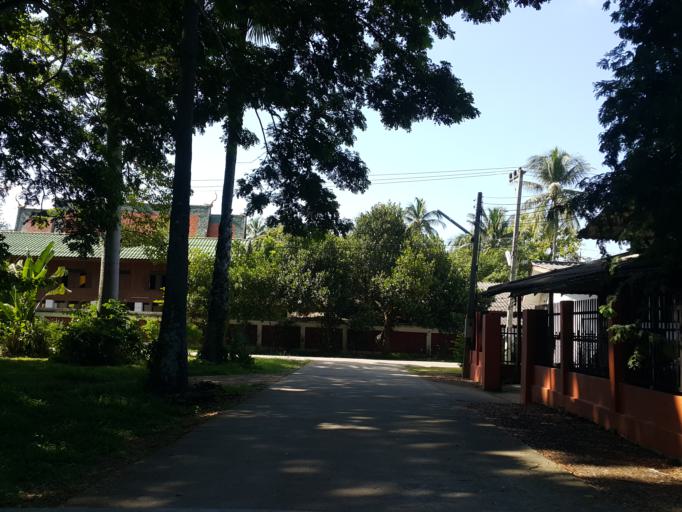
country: TH
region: Chiang Mai
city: San Kamphaeng
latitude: 18.7499
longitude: 99.1716
